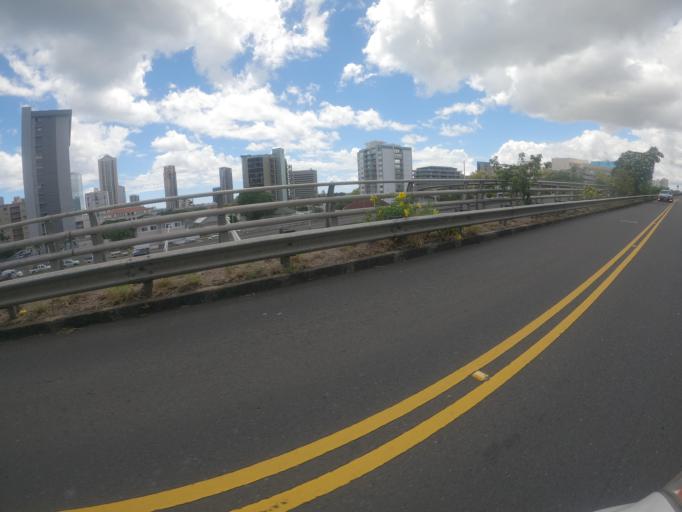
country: US
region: Hawaii
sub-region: Honolulu County
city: Honolulu
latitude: 21.3067
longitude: -157.8499
